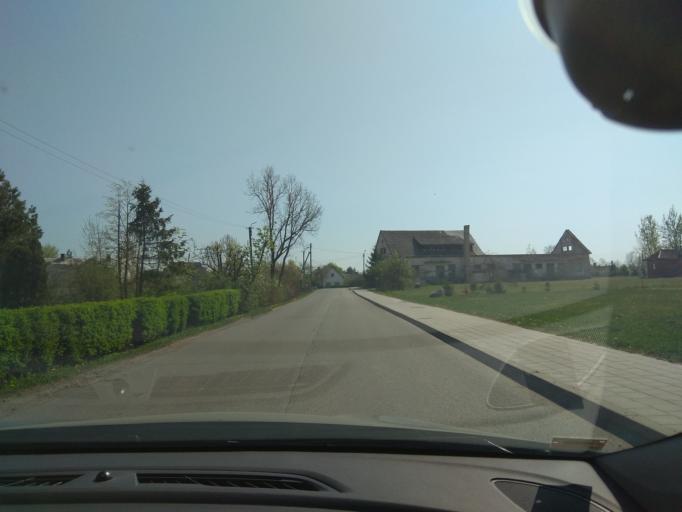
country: LT
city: Linkuva
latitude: 56.0840
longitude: 23.9662
